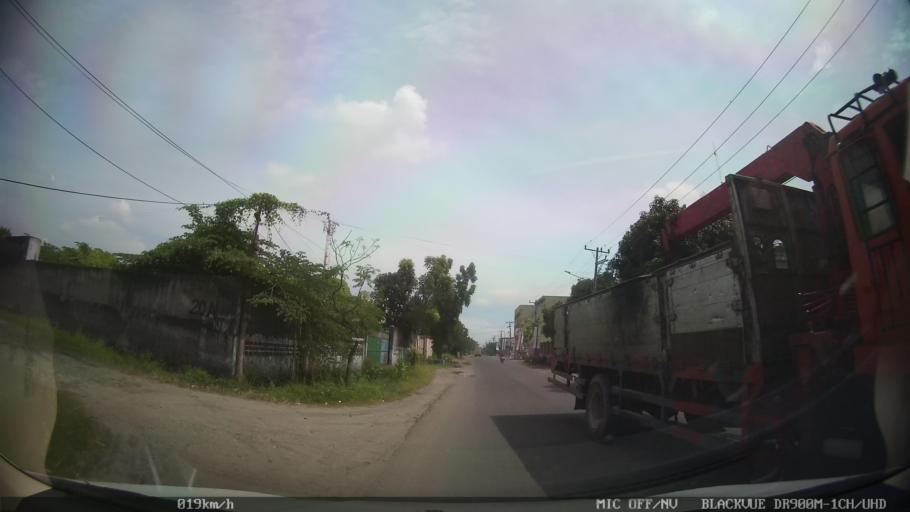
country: ID
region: North Sumatra
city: Medan
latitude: 3.6385
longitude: 98.7164
